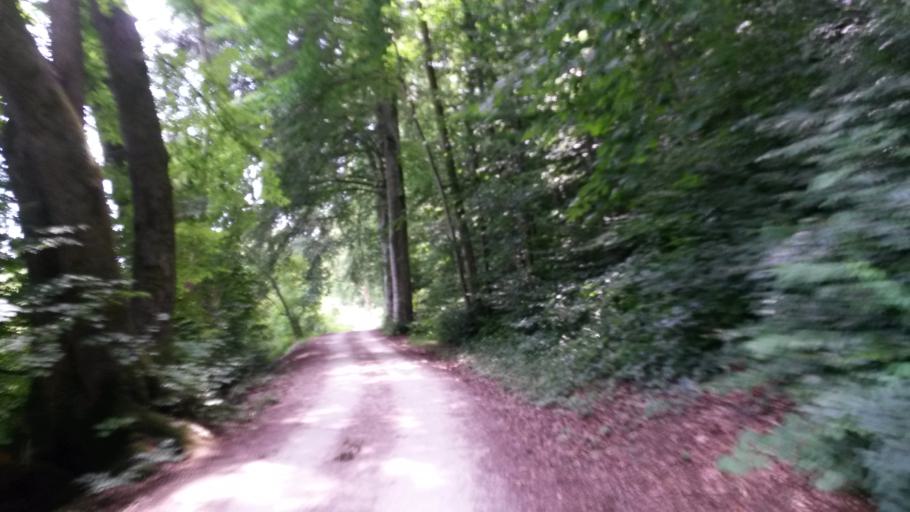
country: DE
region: Bavaria
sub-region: Upper Bavaria
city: Gstadt am Chiemsee
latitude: 47.9069
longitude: 12.4326
